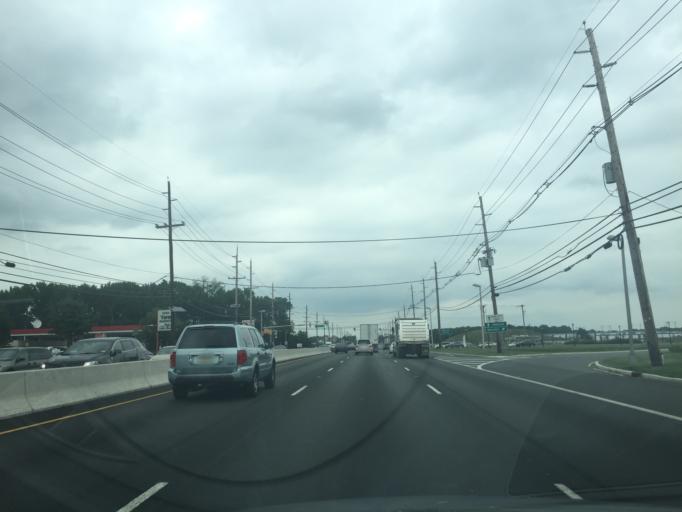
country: US
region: New Jersey
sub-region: Middlesex County
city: Kendall Park
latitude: 40.4374
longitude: -74.5089
